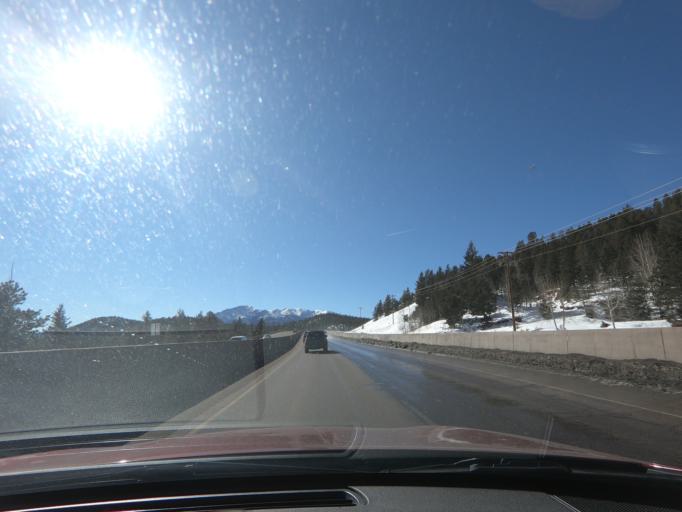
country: US
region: Colorado
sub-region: Teller County
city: Woodland Park
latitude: 38.9872
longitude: -105.0622
